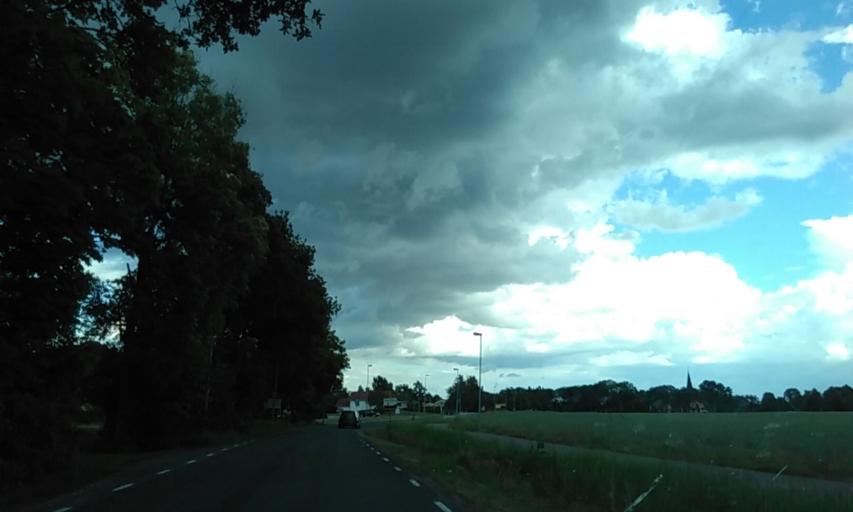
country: SE
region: Vaestra Goetaland
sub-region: Lidkopings Kommun
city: Lidkoping
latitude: 58.5121
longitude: 12.9999
